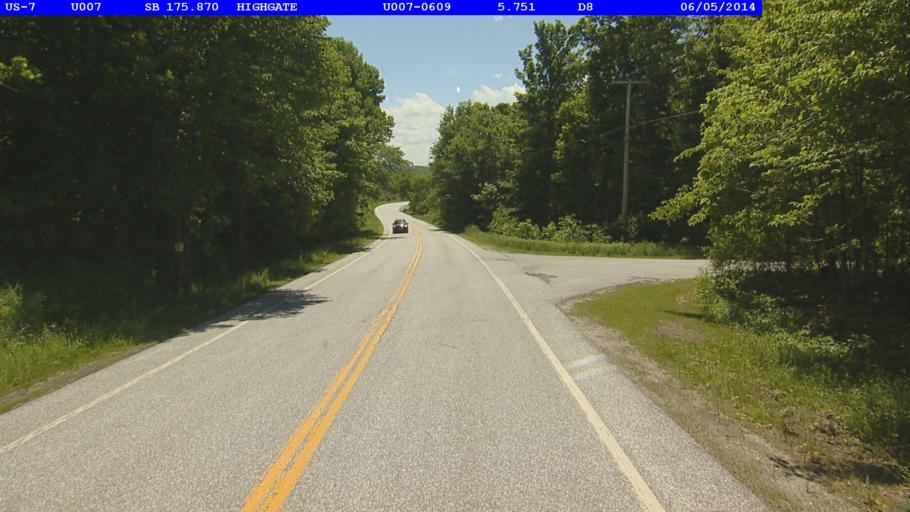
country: US
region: Vermont
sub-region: Franklin County
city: Swanton
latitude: 45.0071
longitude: -73.0823
